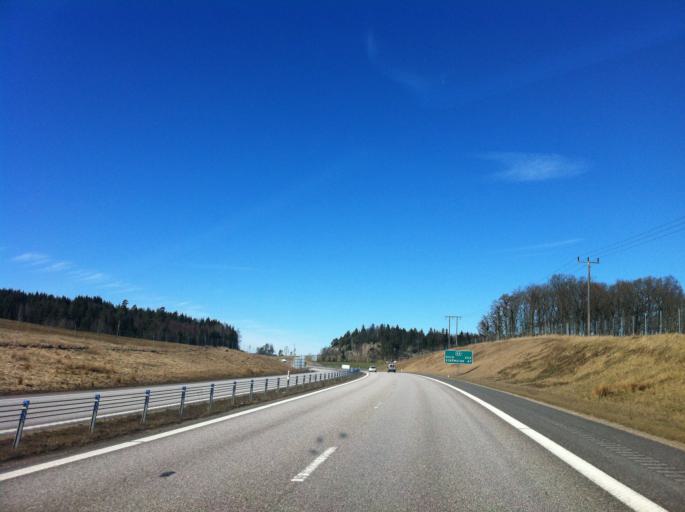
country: SE
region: Vaestra Goetaland
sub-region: Munkedals Kommun
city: Munkedal
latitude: 58.3987
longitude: 11.7490
